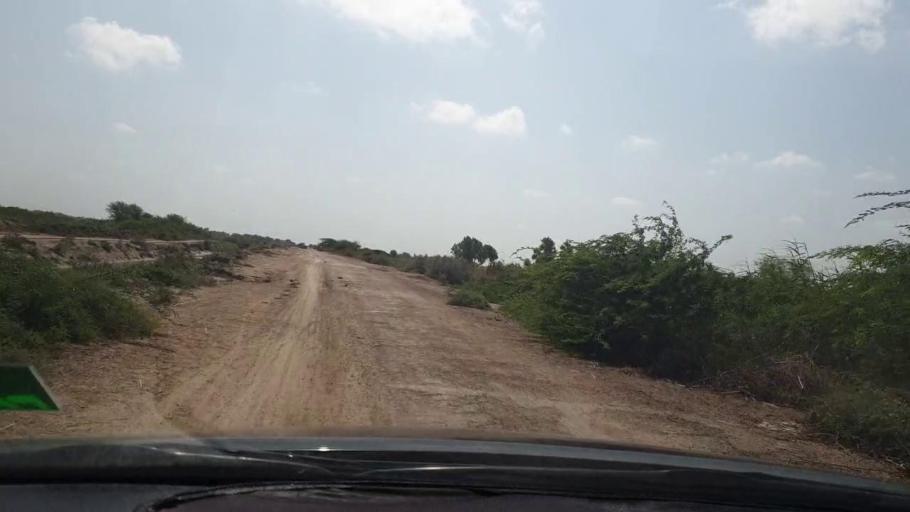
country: PK
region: Sindh
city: Tando Bago
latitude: 24.8475
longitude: 69.0351
